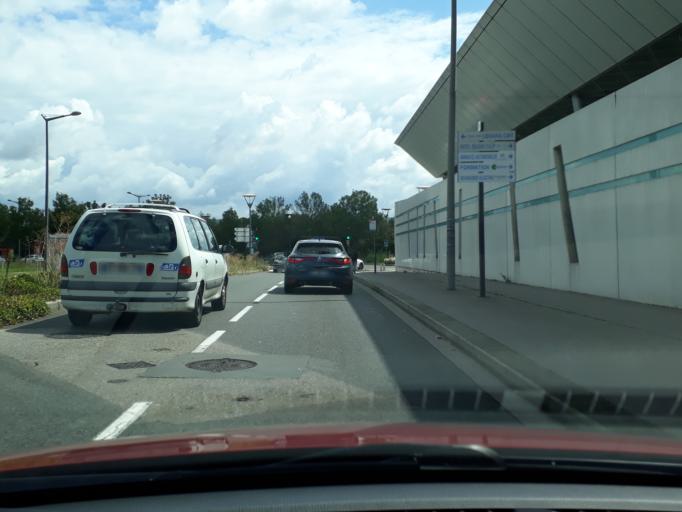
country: FR
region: Rhone-Alpes
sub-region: Departement du Rhone
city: Bron
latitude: 45.7190
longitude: 4.9299
